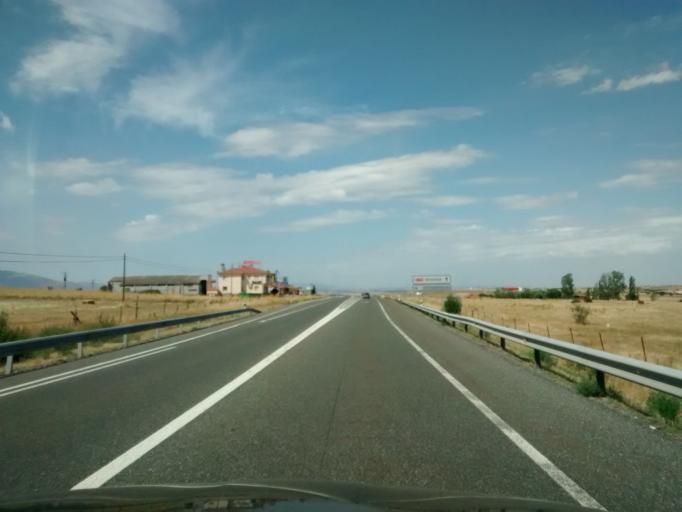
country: ES
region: Castille and Leon
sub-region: Provincia de Segovia
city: Torrecaballeros
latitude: 40.9885
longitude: -4.0358
